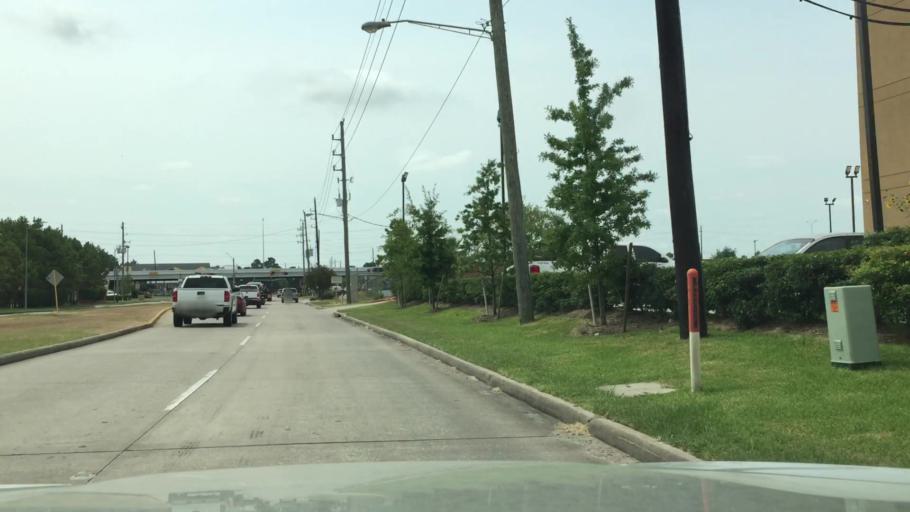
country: US
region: Texas
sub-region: Harris County
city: Jersey Village
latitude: 29.9322
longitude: -95.5456
